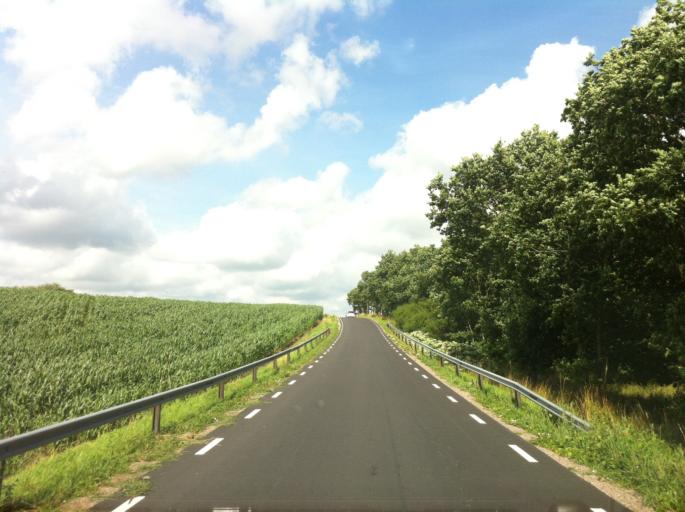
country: SE
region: Skane
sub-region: Trelleborgs Kommun
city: Anderslov
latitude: 55.4482
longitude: 13.3625
